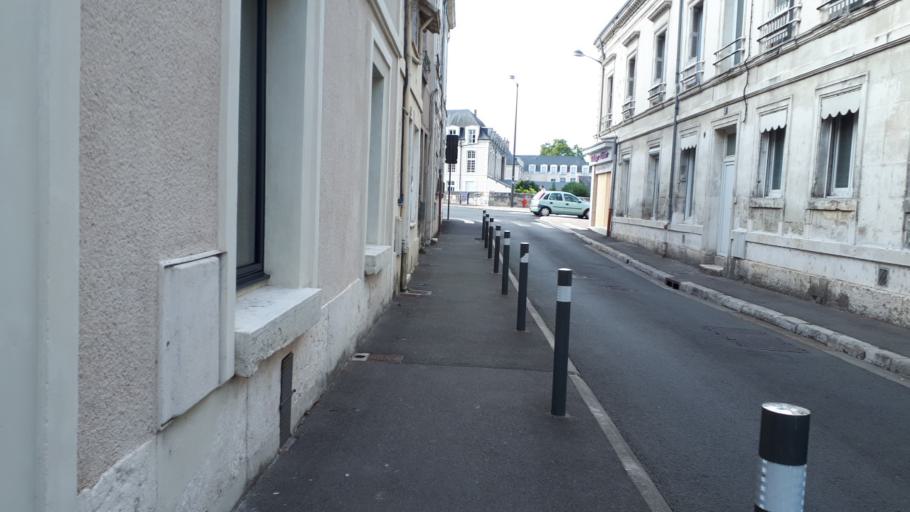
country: FR
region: Centre
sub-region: Departement du Loir-et-Cher
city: Vendome
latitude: 47.7955
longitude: 1.0638
